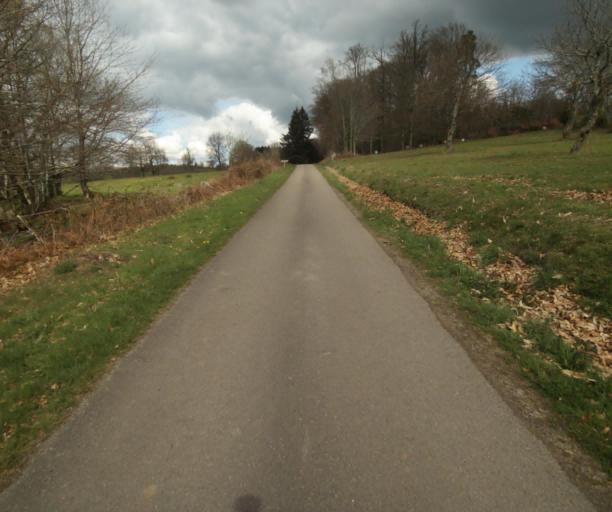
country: FR
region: Limousin
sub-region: Departement de la Correze
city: Correze
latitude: 45.2574
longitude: 1.9027
